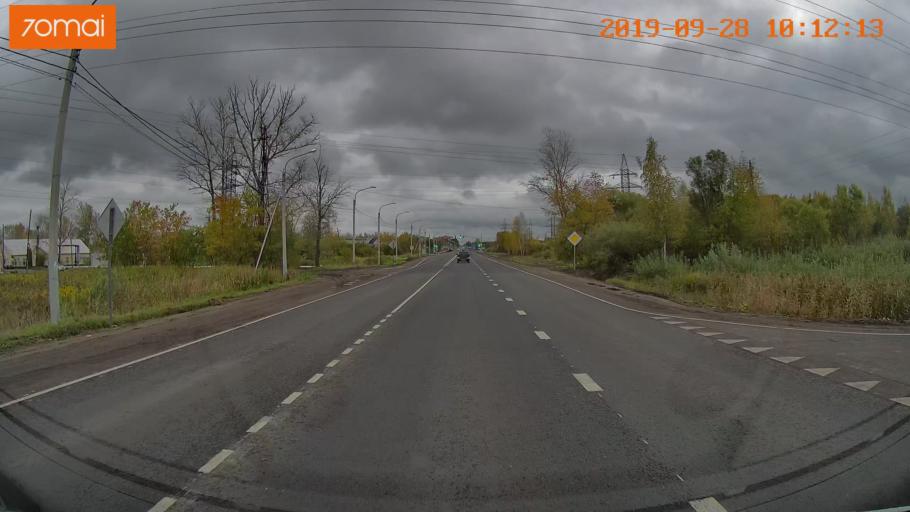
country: RU
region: Jaroslavl
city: Yaroslavl
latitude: 57.5425
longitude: 39.9532
